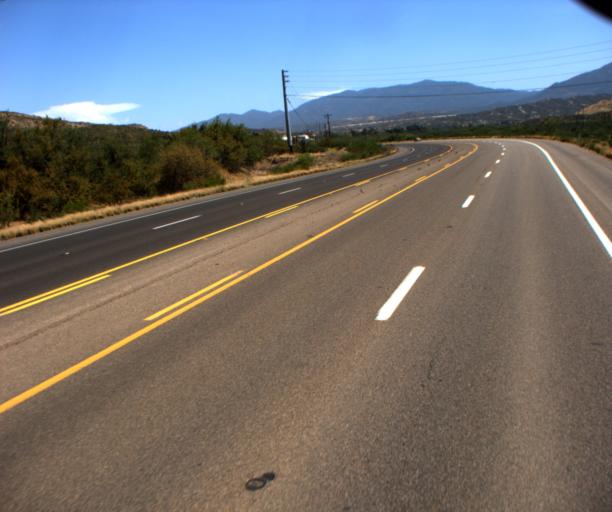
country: US
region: Arizona
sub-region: Gila County
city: Claypool
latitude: 33.4379
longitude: -110.8291
